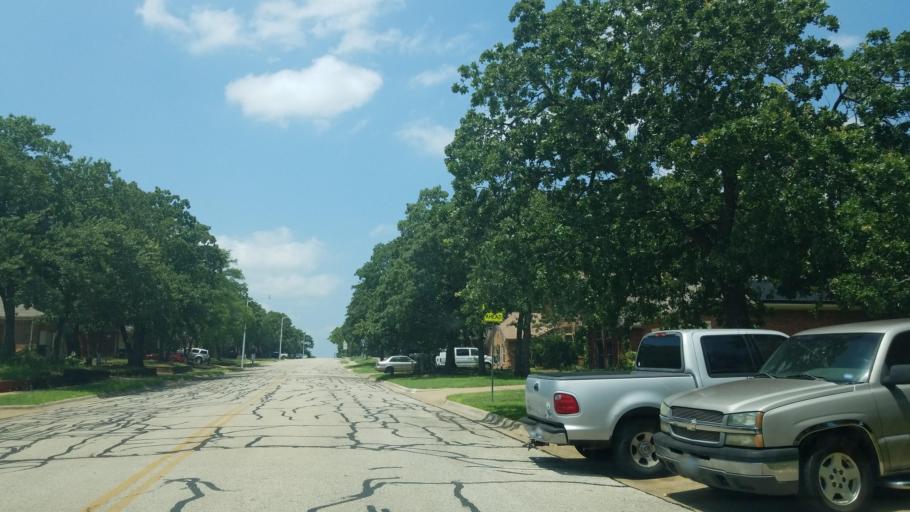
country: US
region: Texas
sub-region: Denton County
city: Denton
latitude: 33.2179
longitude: -97.1060
